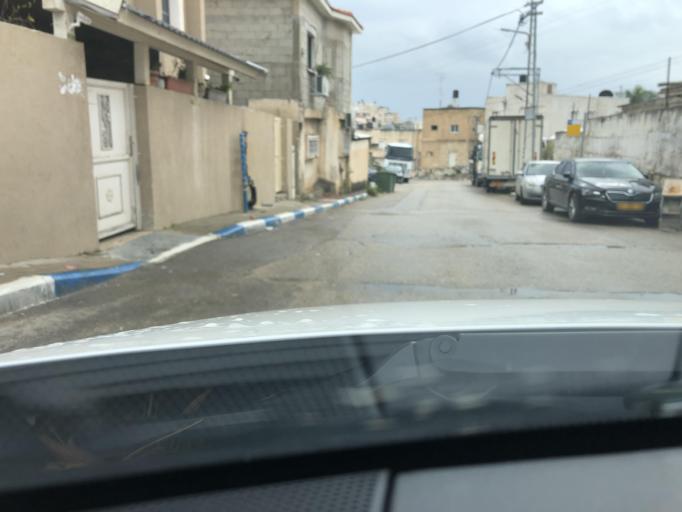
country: IL
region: Central District
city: Kafr Qasim
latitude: 32.1129
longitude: 34.9757
